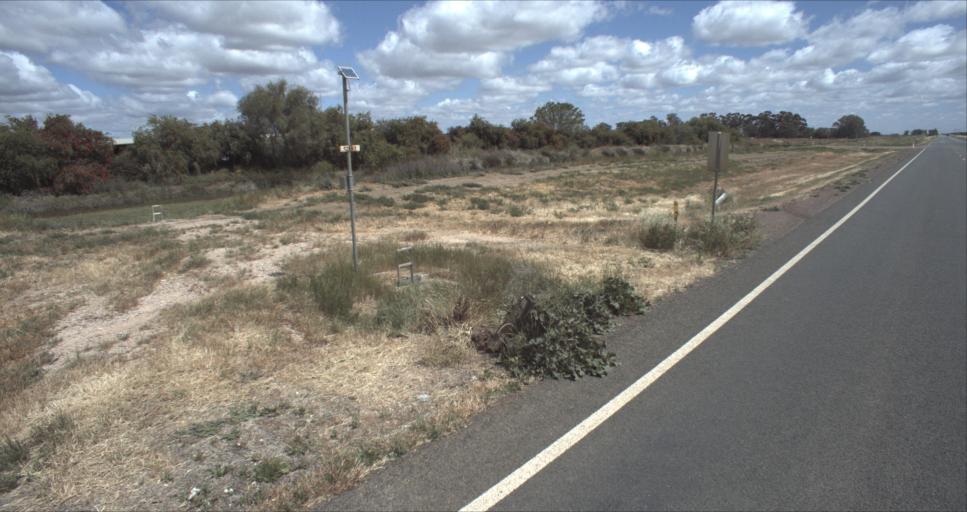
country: AU
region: New South Wales
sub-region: Murrumbidgee Shire
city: Darlington Point
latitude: -34.4870
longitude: 146.1608
